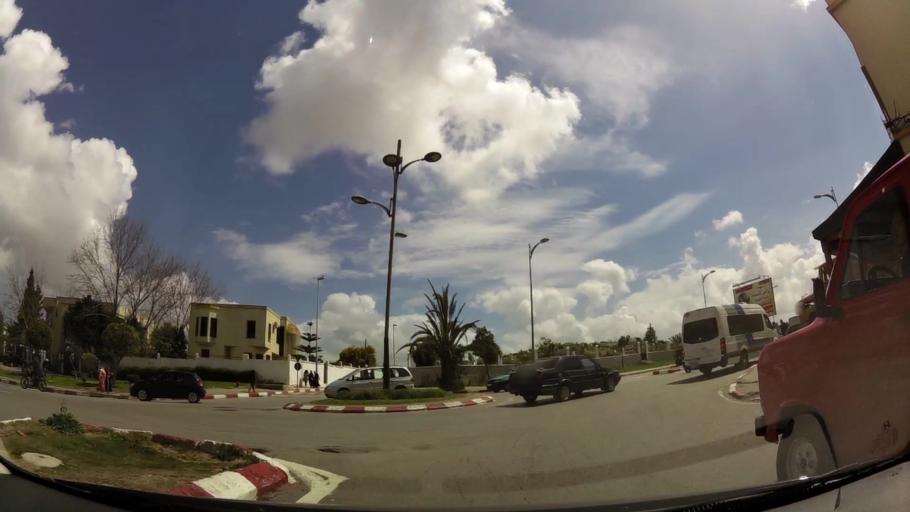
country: MA
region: Tanger-Tetouan
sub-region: Tanger-Assilah
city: Tangier
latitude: 35.7505
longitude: -5.8294
